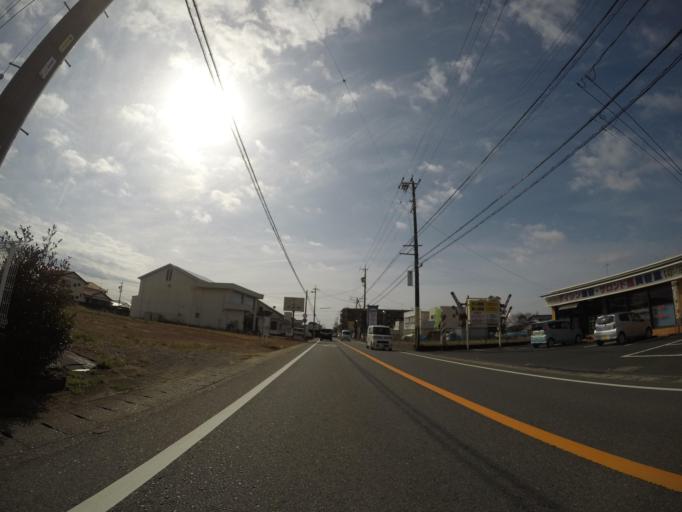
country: JP
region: Shizuoka
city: Hamakita
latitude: 34.7966
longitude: 137.7003
